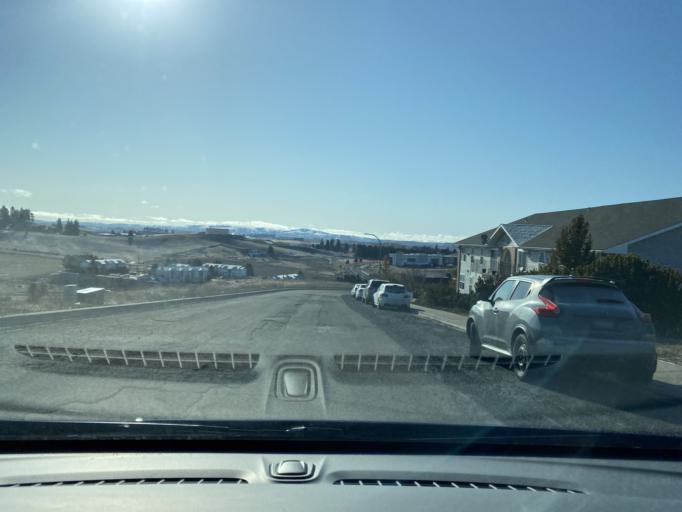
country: US
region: Washington
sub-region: Whitman County
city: Pullman
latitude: 46.7461
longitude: -117.1515
